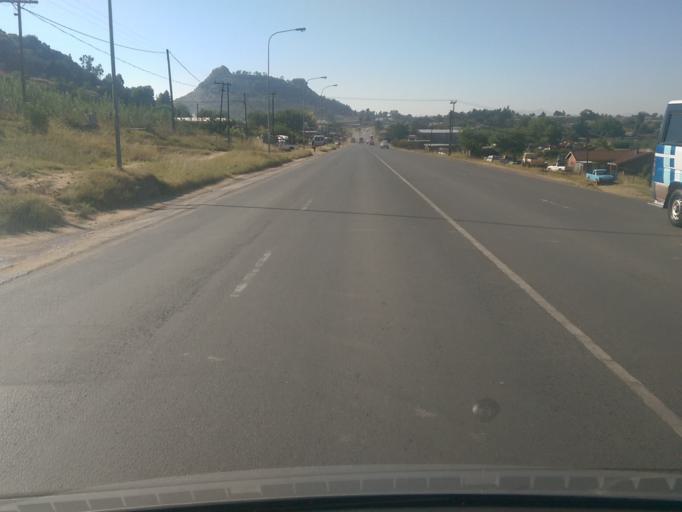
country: LS
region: Maseru
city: Maseru
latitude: -29.3541
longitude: 27.5227
